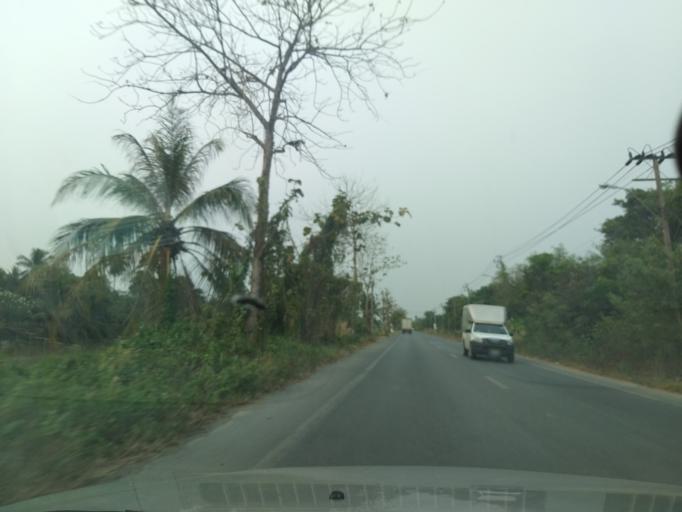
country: TH
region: Bangkok
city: Nong Chok
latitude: 13.9323
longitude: 100.8935
